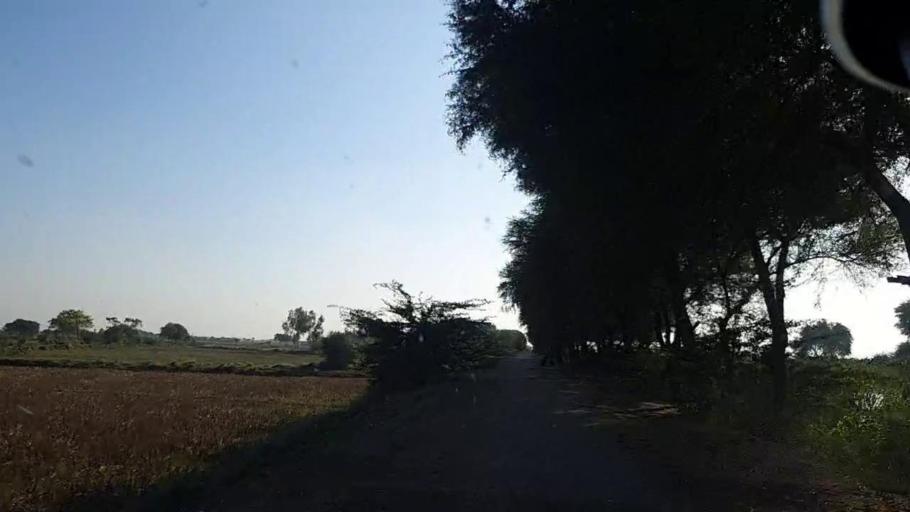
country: PK
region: Sindh
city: Chuhar Jamali
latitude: 24.5649
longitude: 68.0410
